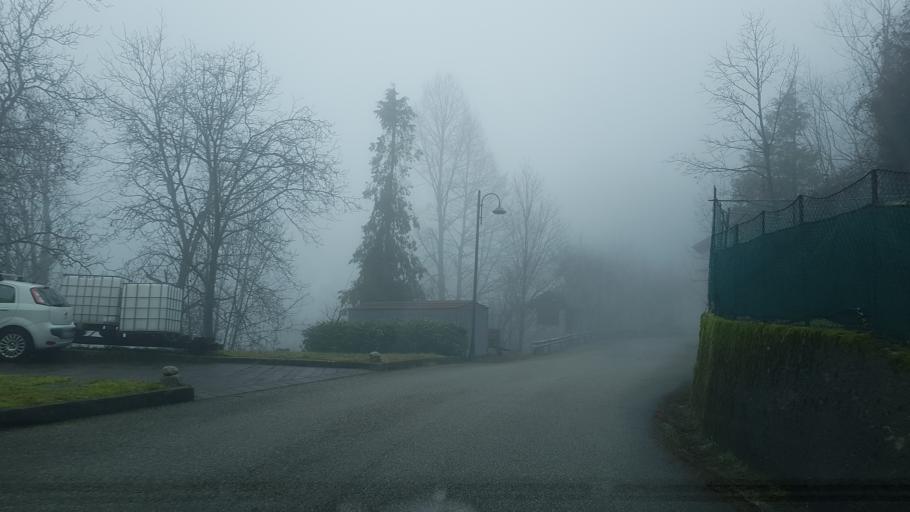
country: IT
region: Friuli Venezia Giulia
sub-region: Provincia di Udine
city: Stregna
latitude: 46.1225
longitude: 13.6021
